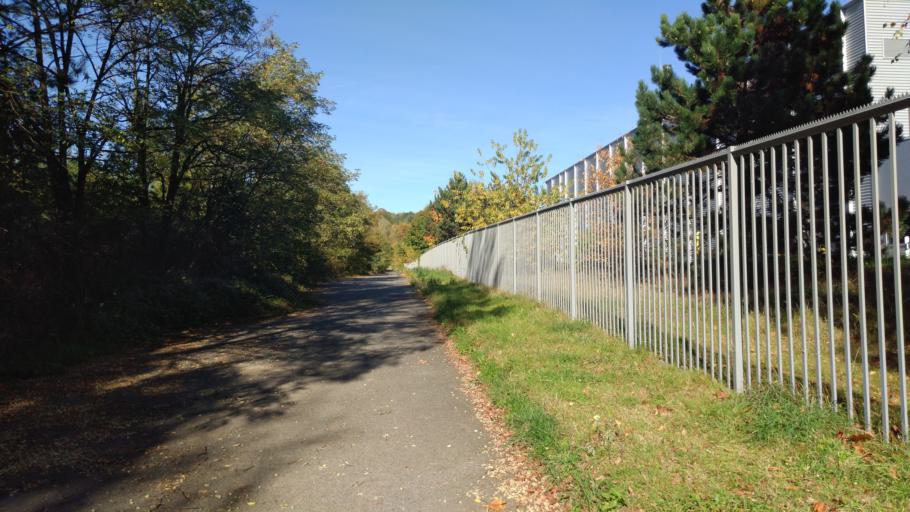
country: DE
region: Saxony
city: Albertstadt
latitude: 51.0997
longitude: 13.7303
